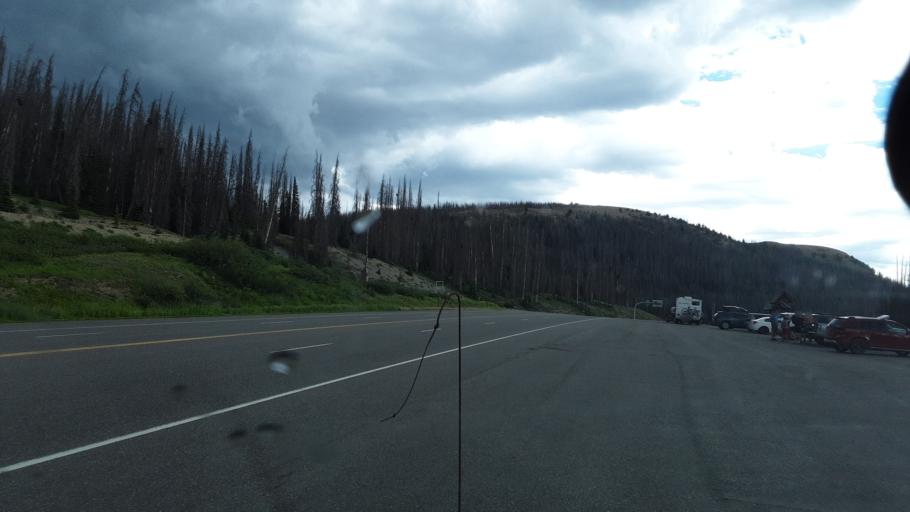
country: US
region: Colorado
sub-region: Archuleta County
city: Pagosa Springs
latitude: 37.4830
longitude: -106.8033
